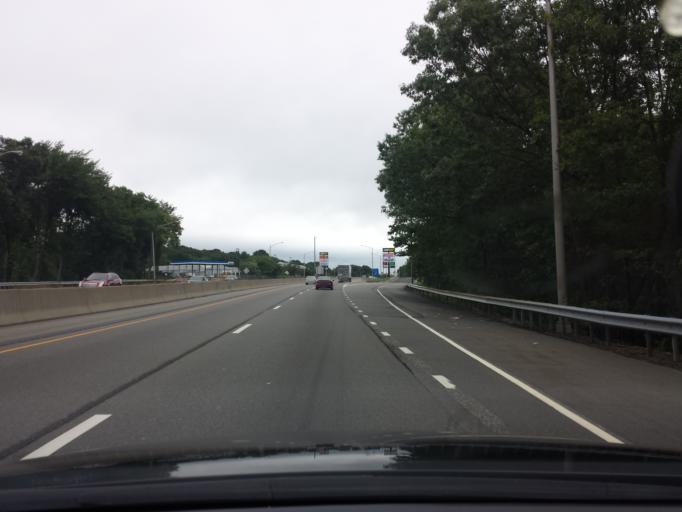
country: US
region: Connecticut
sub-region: New Haven County
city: Madison
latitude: 41.2910
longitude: -72.5842
